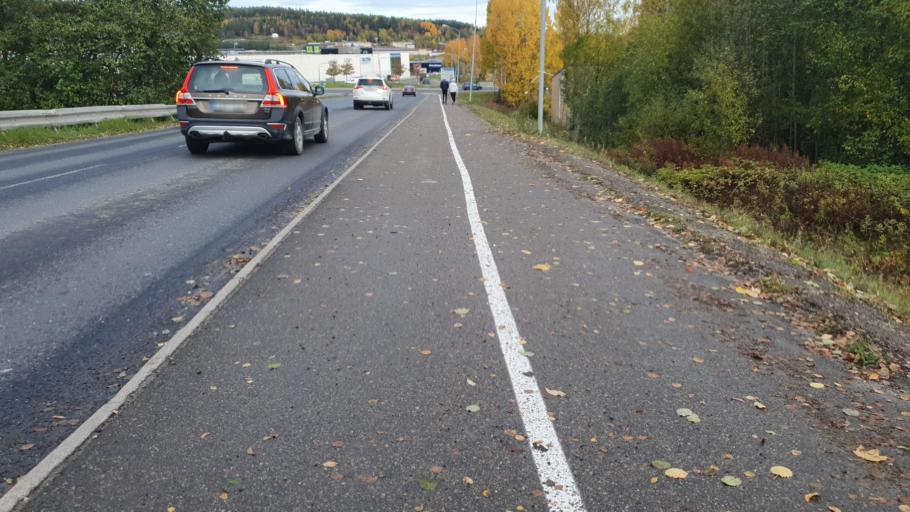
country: SE
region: Vaesternorrland
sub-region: Sundsvalls Kommun
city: Sundsbruk
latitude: 62.4396
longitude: 17.3404
